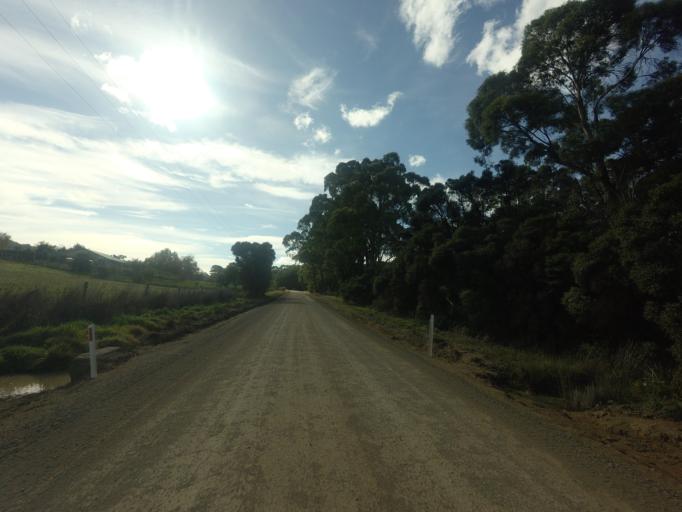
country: AU
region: Tasmania
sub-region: Clarence
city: Sandford
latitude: -43.1609
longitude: 147.7683
